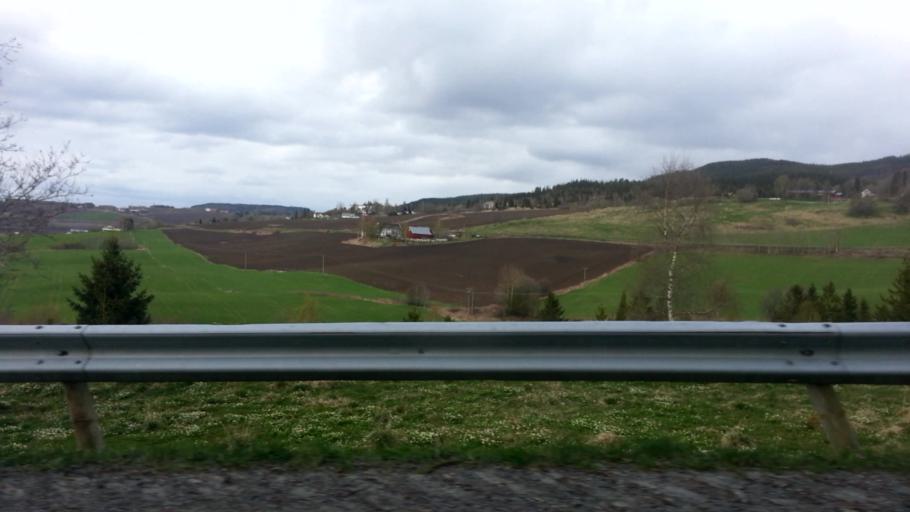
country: NO
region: Nord-Trondelag
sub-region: Levanger
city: Skogn
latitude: 63.6614
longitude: 11.2296
